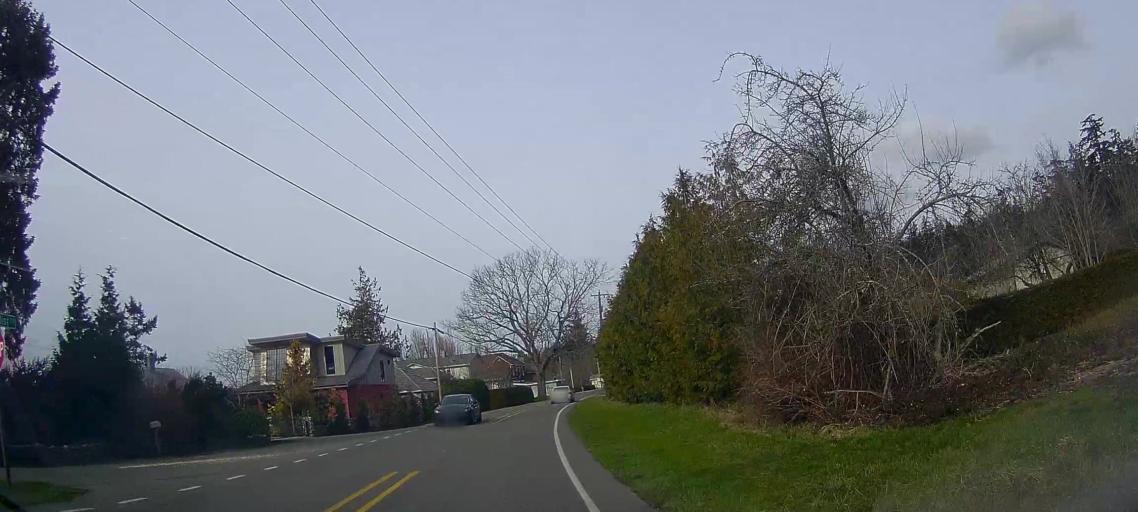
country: US
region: Washington
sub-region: Island County
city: Camano
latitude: 48.1719
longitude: -122.5283
